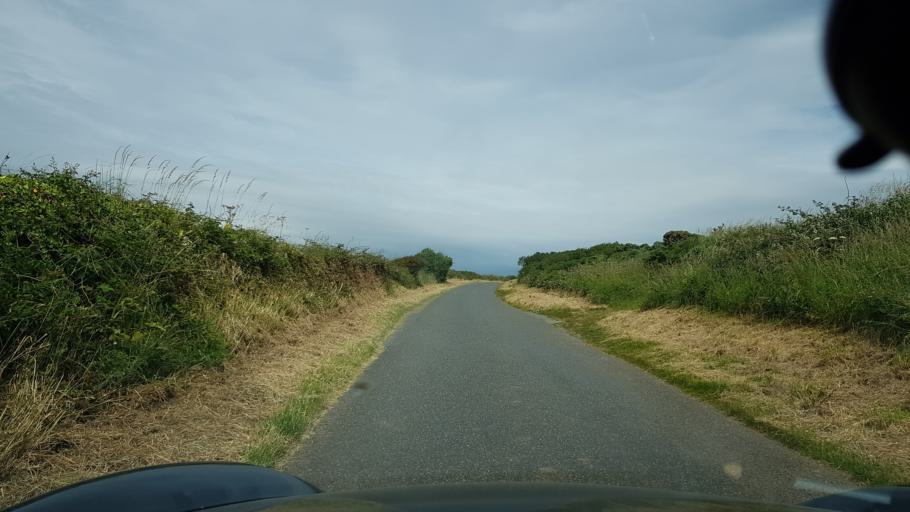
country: GB
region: Wales
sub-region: Pembrokeshire
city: Dale
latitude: 51.7320
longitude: -5.2167
